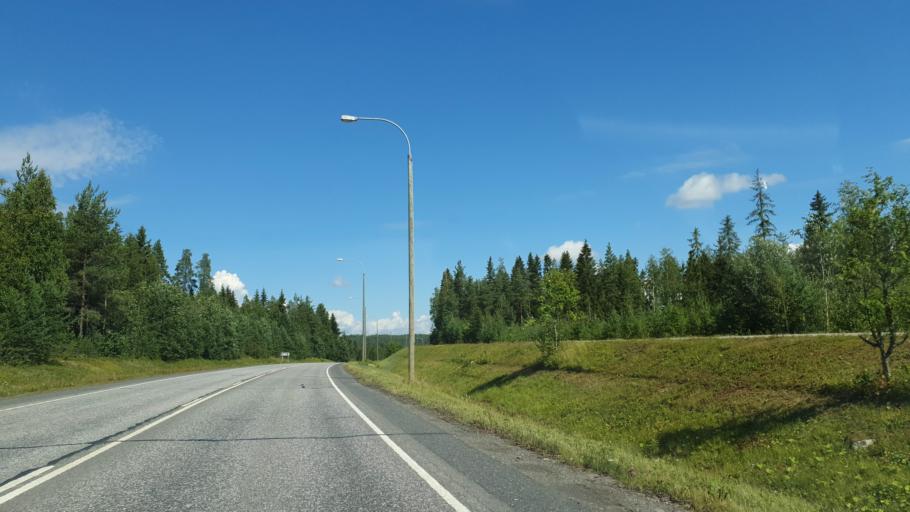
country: FI
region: Northern Savo
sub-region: Ylae-Savo
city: Iisalmi
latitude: 63.6325
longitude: 27.2253
